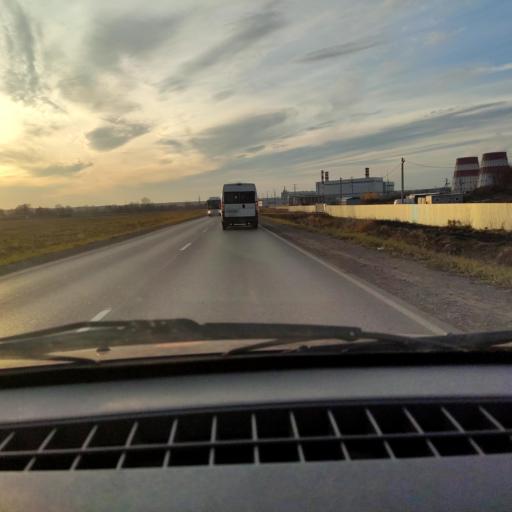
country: RU
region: Bashkortostan
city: Mikhaylovka
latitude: 54.7992
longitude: 55.8522
